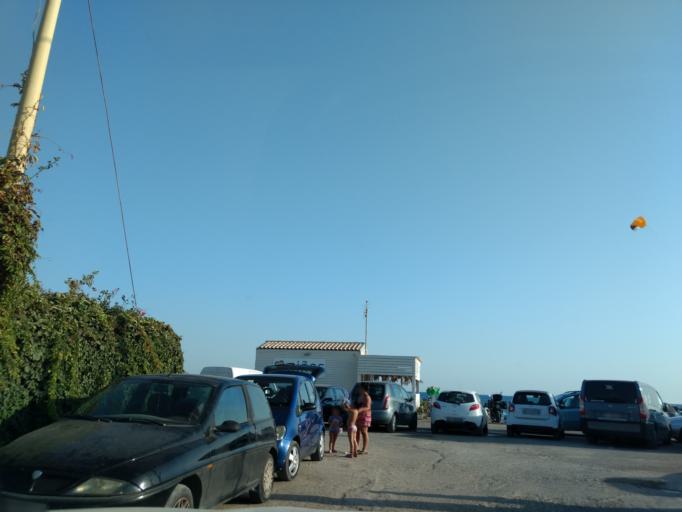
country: IT
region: Sicily
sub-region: Ragusa
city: Donnalucata
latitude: 36.7470
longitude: 14.6628
